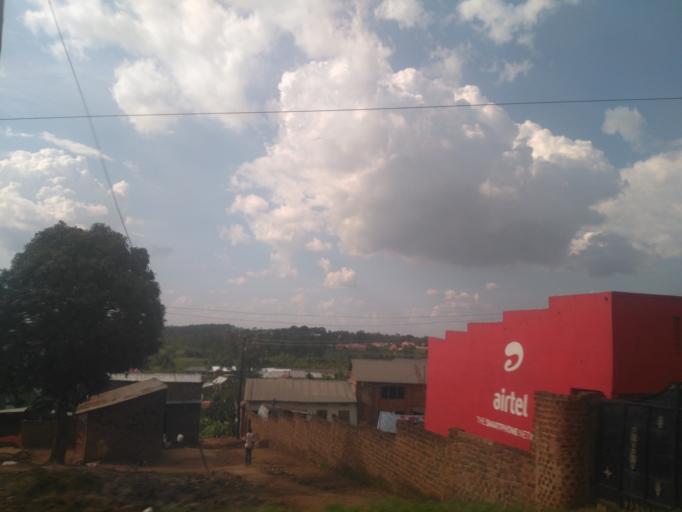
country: UG
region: Central Region
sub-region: Wakiso District
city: Kajansi
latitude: 0.2781
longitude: 32.4458
